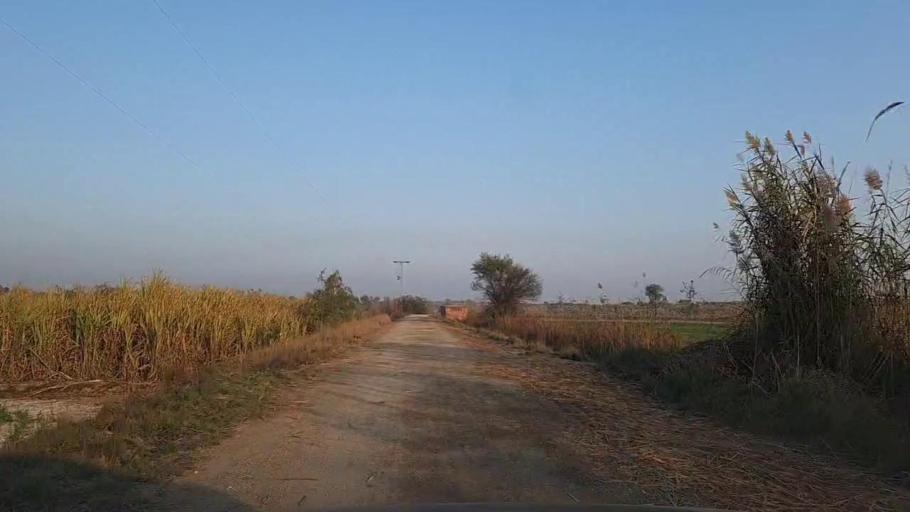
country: PK
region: Sindh
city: Daur
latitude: 26.4873
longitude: 68.4268
